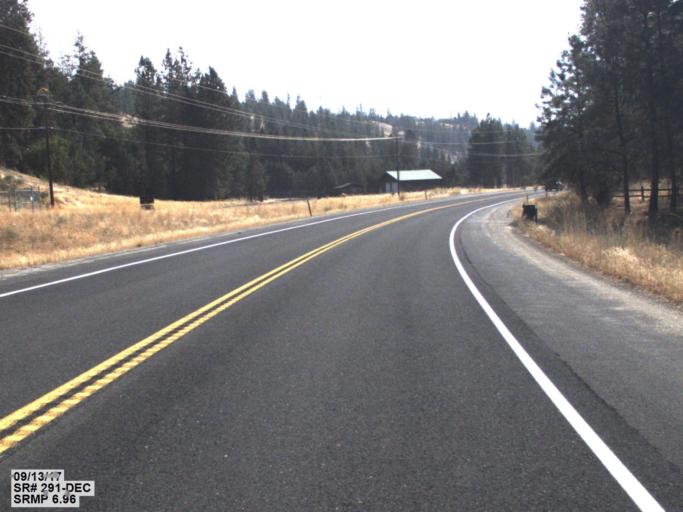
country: US
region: Washington
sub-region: Spokane County
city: Fairwood
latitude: 47.7587
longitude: -117.5215
